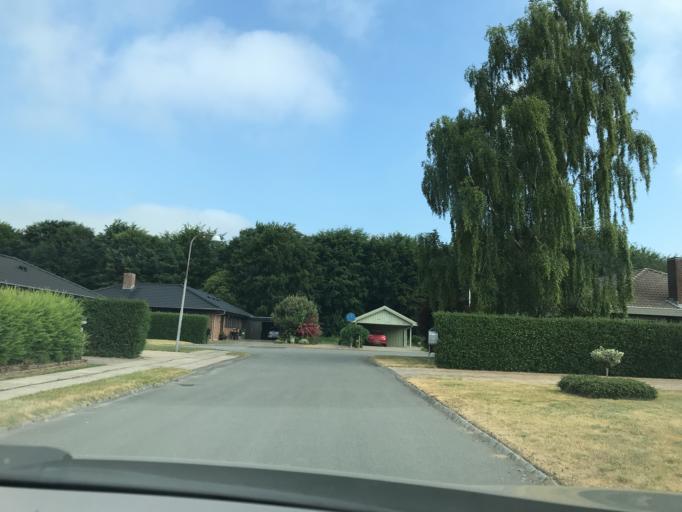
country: DK
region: South Denmark
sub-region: Odense Kommune
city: Bellinge
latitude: 55.3756
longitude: 10.3439
